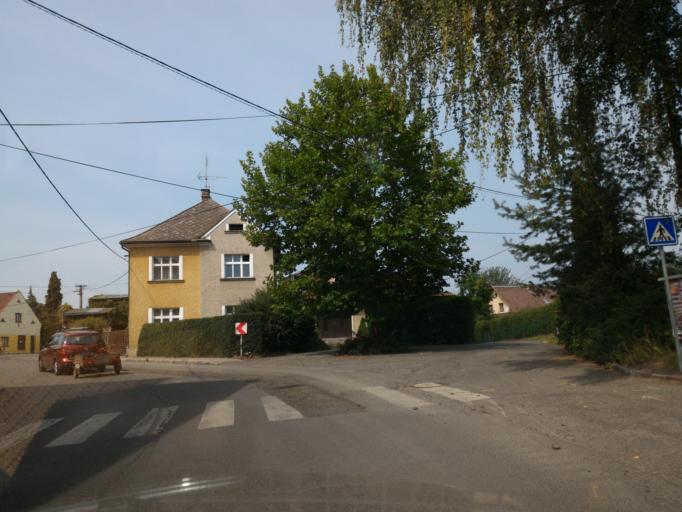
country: CZ
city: Ohrazenice
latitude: 50.5830
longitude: 15.1127
